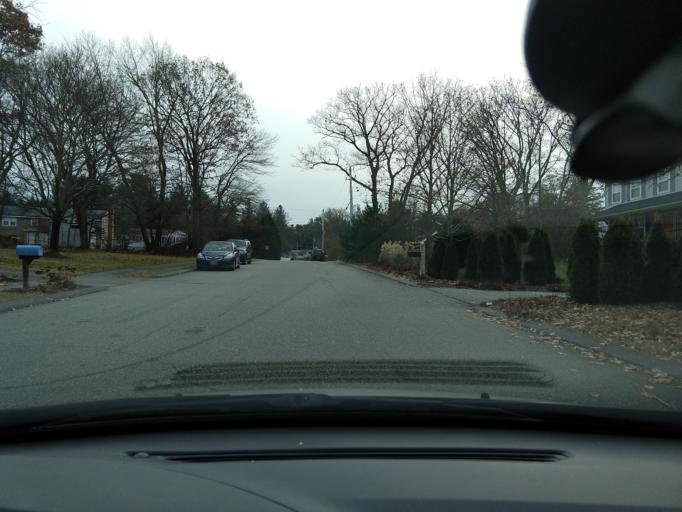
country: US
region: Massachusetts
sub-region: Middlesex County
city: Billerica
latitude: 42.5644
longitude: -71.2761
